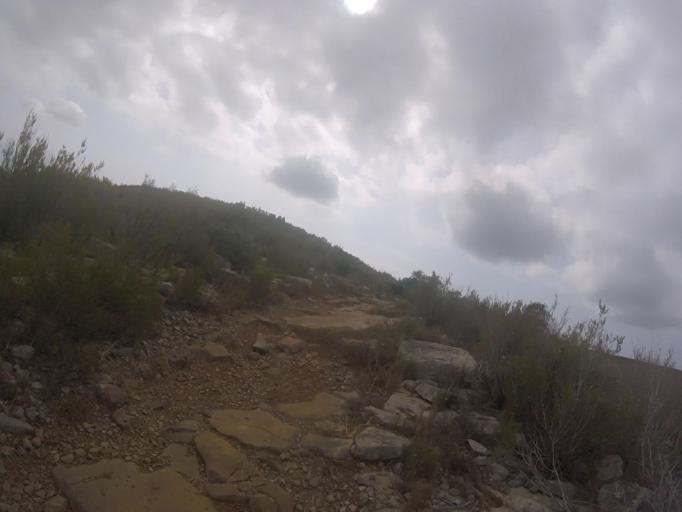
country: ES
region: Valencia
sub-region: Provincia de Castello
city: Santa Magdalena de Pulpis
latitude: 40.3477
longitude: 0.3464
